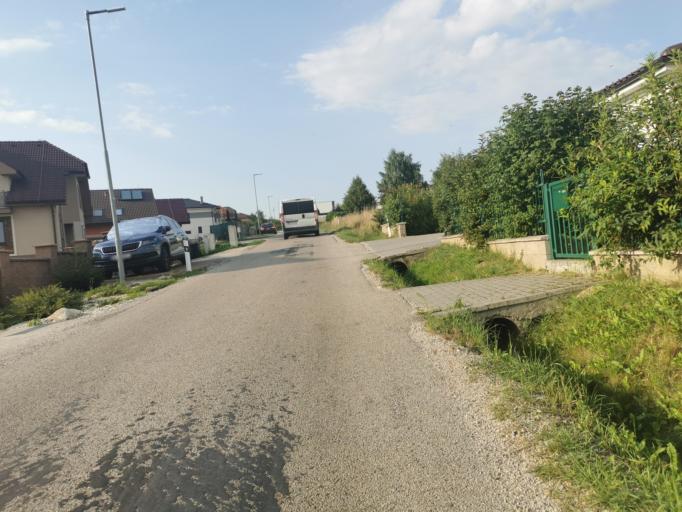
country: SK
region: Trenciansky
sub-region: Okres Myjava
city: Myjava
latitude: 48.7787
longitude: 17.5656
